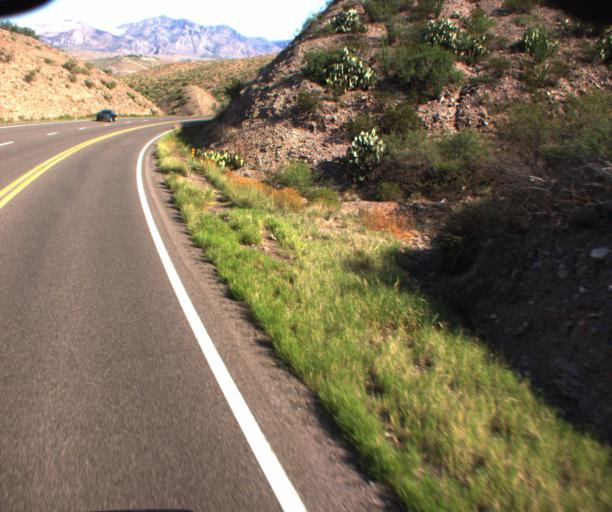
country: US
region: Arizona
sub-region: Greenlee County
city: Clifton
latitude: 33.0220
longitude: -109.2920
